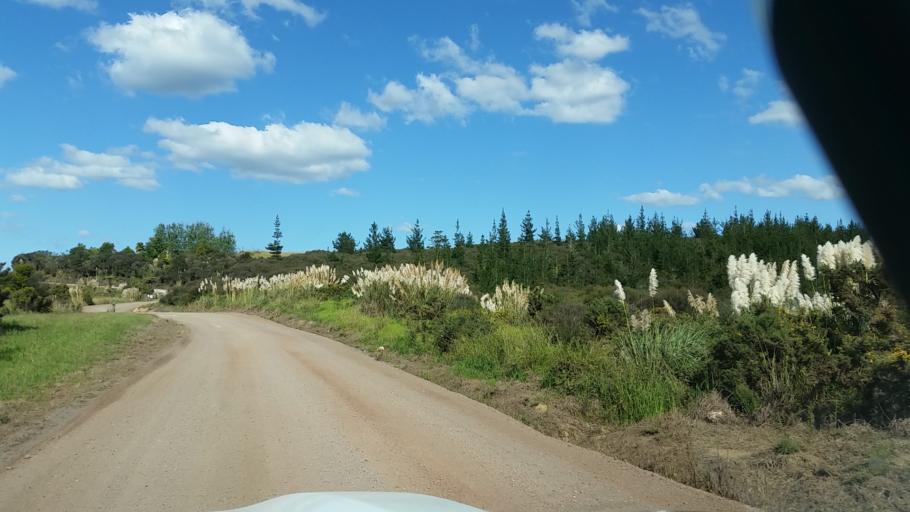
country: NZ
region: Northland
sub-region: Whangarei
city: Whangarei
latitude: -35.5877
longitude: 174.3147
